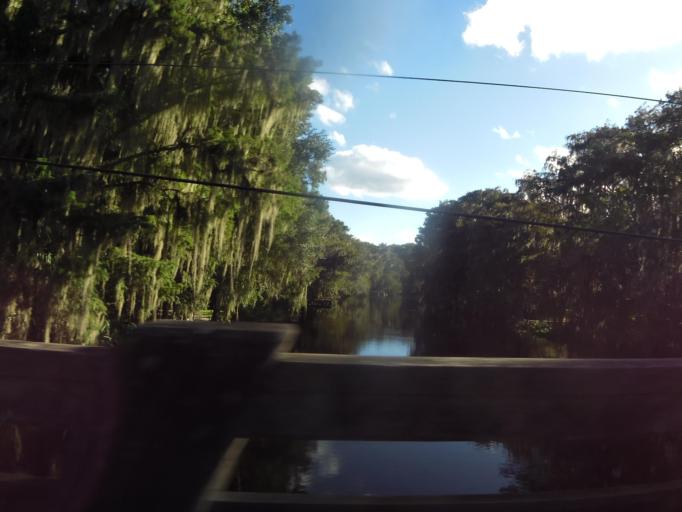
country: US
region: Florida
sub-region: Marion County
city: Citra
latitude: 29.4864
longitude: -82.1653
